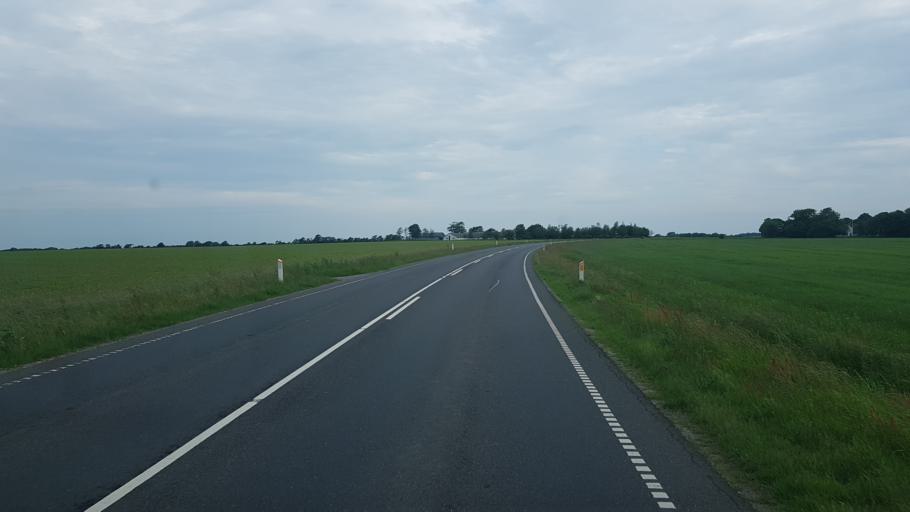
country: DK
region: South Denmark
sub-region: Vejen Kommune
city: Rodding
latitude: 55.4000
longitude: 9.0344
